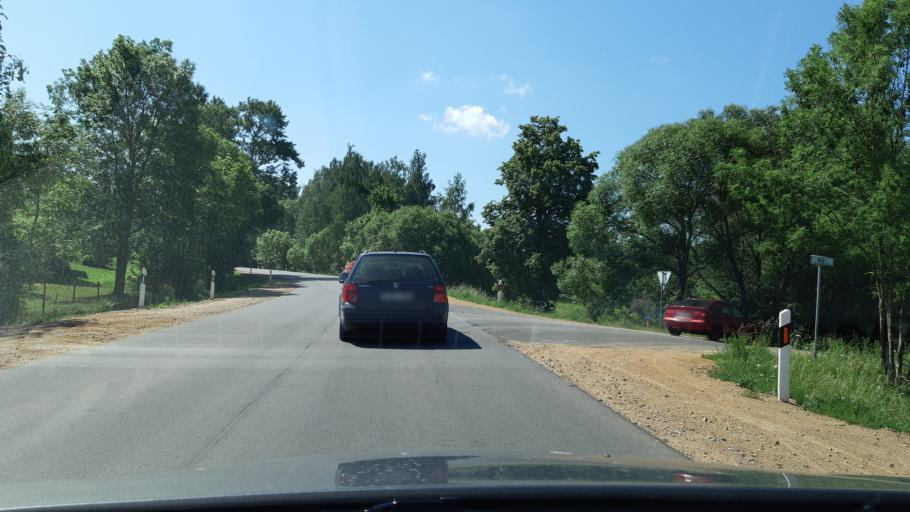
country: LT
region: Kauno apskritis
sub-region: Kauno rajonas
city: Karmelava
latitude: 54.8426
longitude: 24.2356
